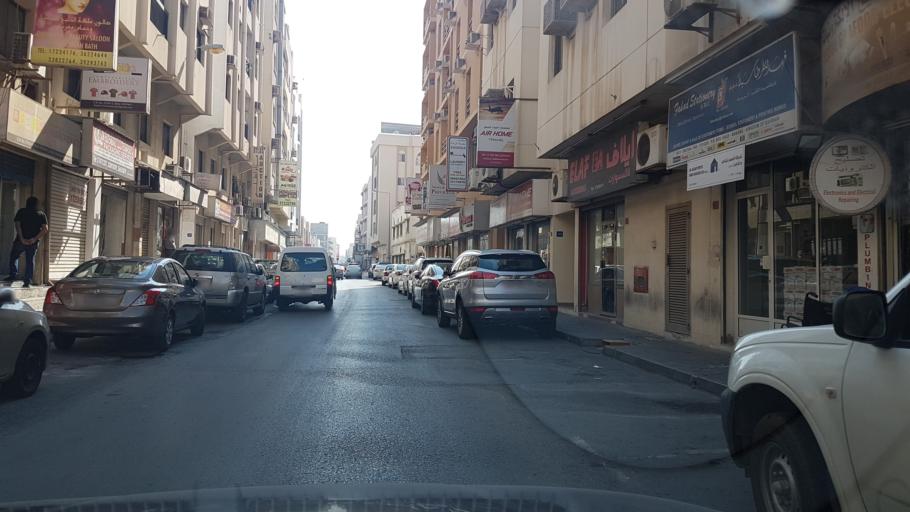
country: BH
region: Manama
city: Manama
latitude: 26.2314
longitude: 50.5810
